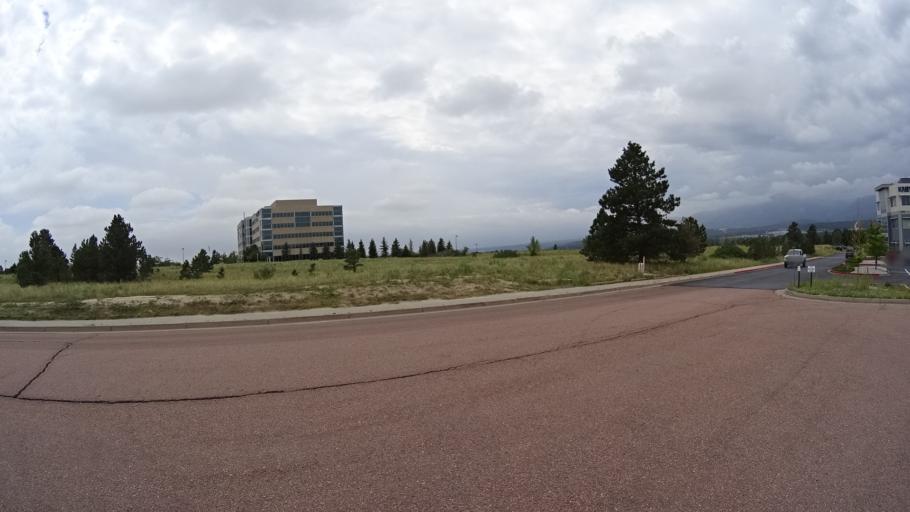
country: US
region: Colorado
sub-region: El Paso County
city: Gleneagle
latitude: 39.0128
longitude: -104.8200
